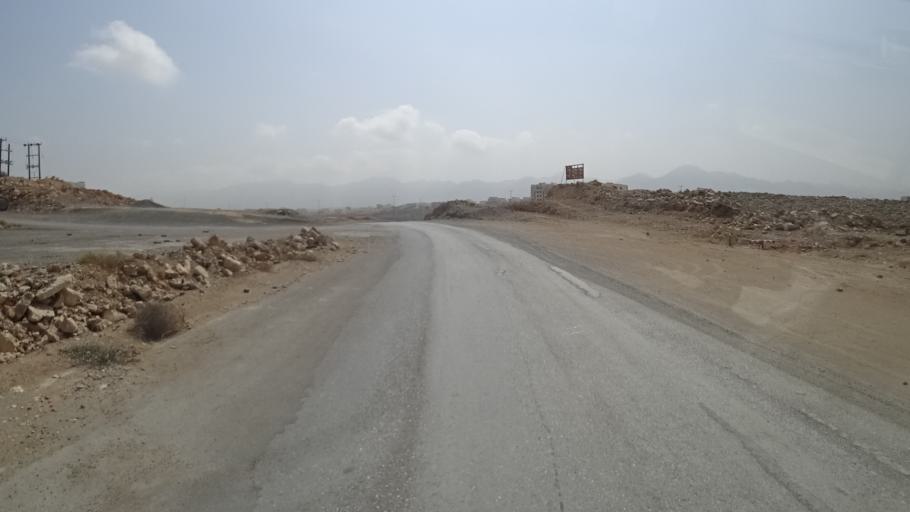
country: OM
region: Muhafazat Masqat
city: Bawshar
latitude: 23.5645
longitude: 58.3421
